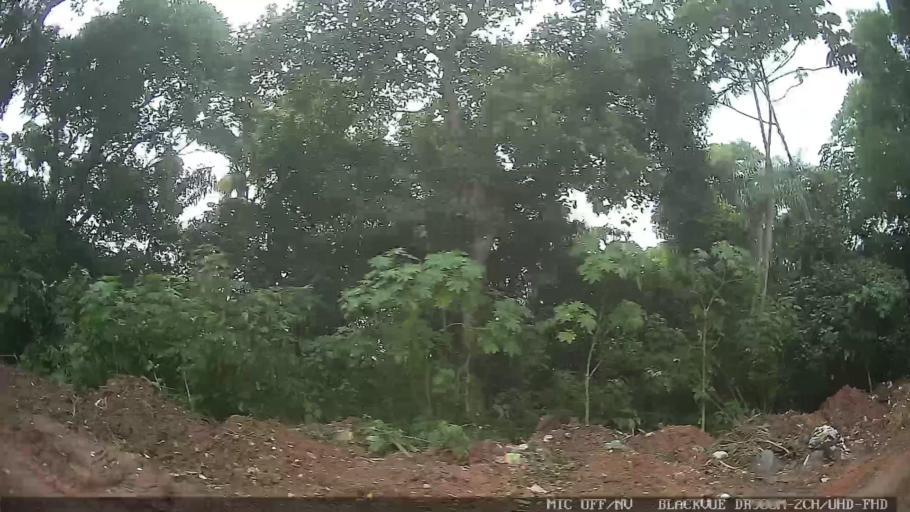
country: BR
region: Sao Paulo
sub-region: Itaquaquecetuba
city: Itaquaquecetuba
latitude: -23.4675
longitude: -46.2999
